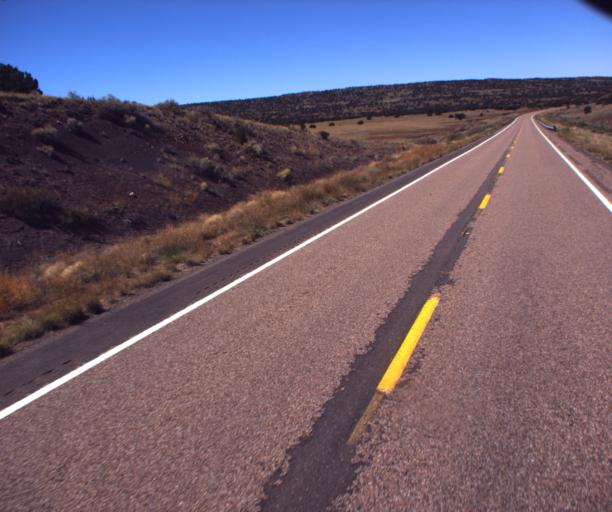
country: US
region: Arizona
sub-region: Apache County
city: Saint Johns
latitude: 34.5699
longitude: -109.5168
